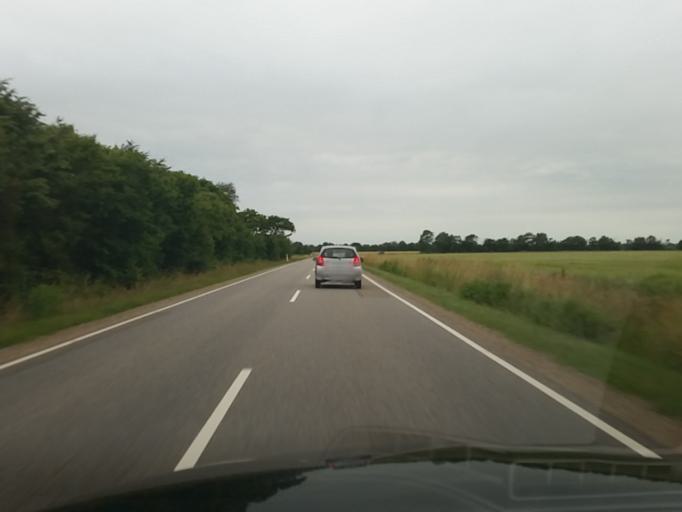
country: DK
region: South Denmark
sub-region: Billund Kommune
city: Grindsted
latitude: 55.6636
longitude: 8.7613
